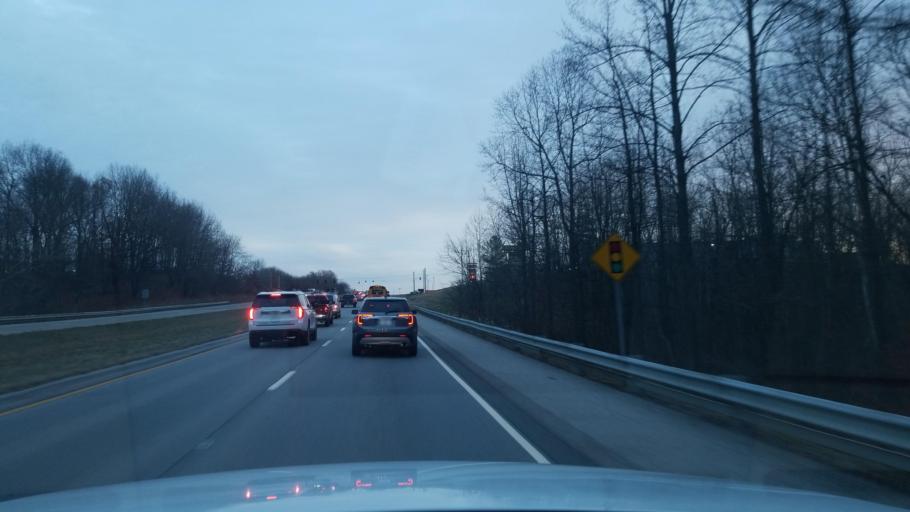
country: US
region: Indiana
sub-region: Vanderburgh County
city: Evansville
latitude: 37.9736
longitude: -87.6495
